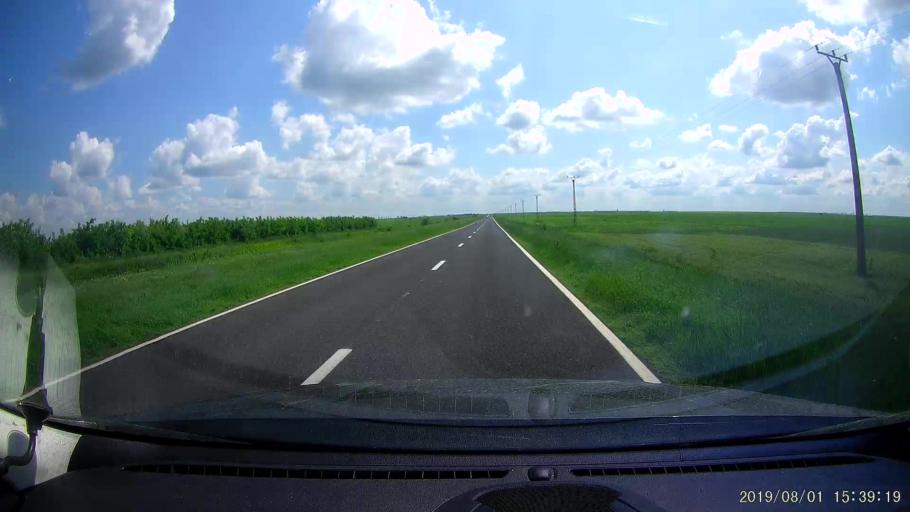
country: RO
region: Braila
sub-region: Comuna Insuratei
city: Insuratei
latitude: 44.8605
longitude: 27.5620
